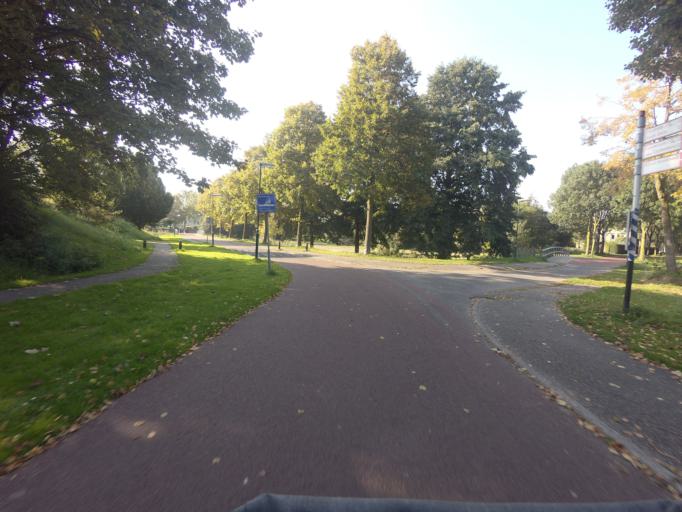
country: NL
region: Utrecht
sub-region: Gemeente Houten
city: Houten
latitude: 52.0328
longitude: 5.1557
